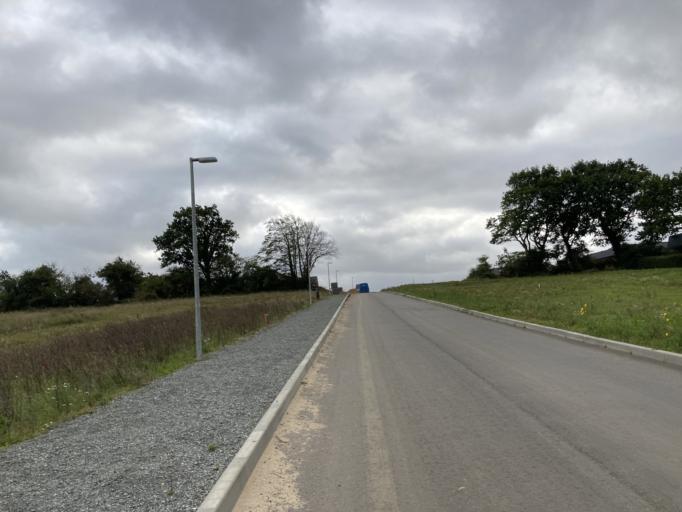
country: DK
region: South Denmark
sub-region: Kolding Kommune
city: Sonder Bjert
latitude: 55.4515
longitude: 9.5621
